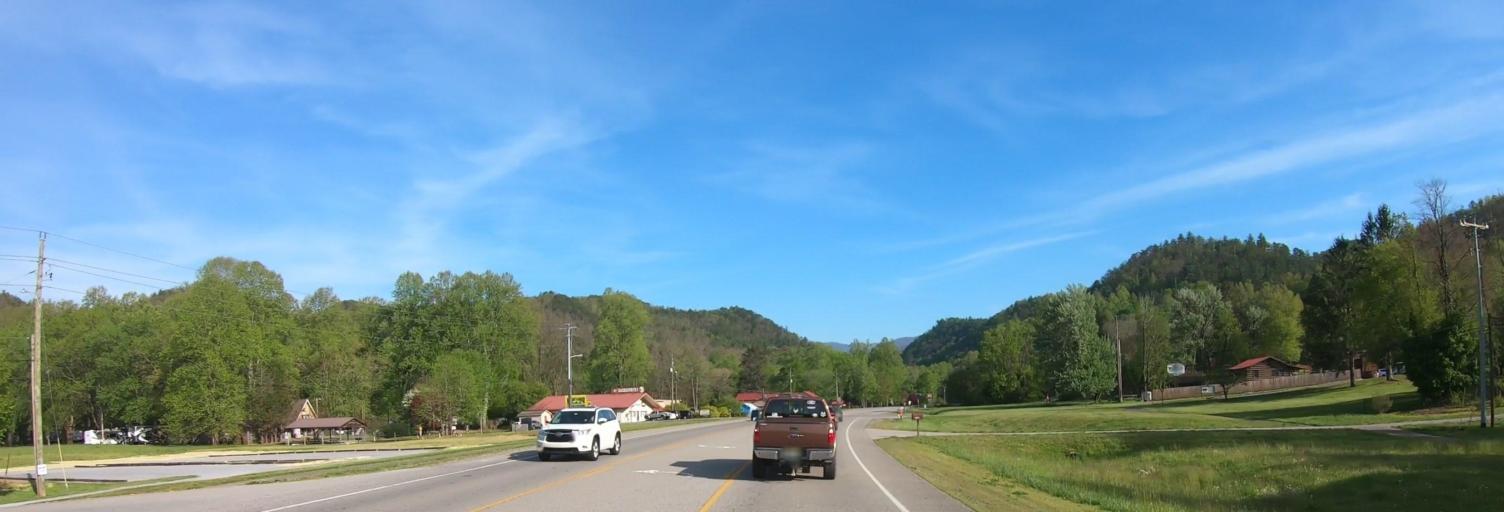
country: US
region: Tennessee
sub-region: Blount County
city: Wildwood
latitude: 35.6780
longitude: -83.7203
